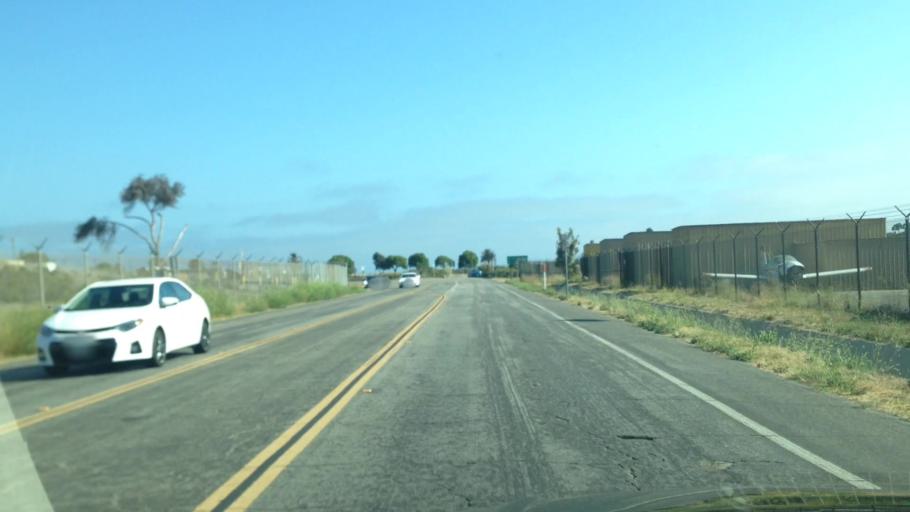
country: US
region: California
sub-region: Santa Barbara County
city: Goleta
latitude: 34.4206
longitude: -119.8352
